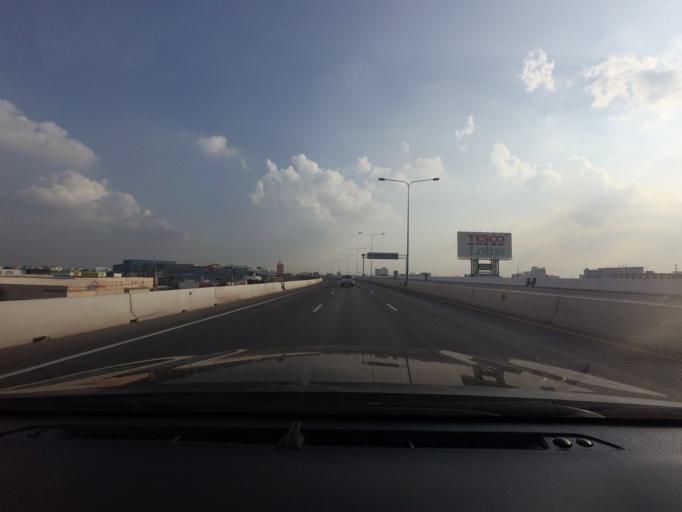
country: TH
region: Phra Nakhon Si Ayutthaya
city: Ban Bang Kadi Pathum Thani
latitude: 13.9943
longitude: 100.6148
